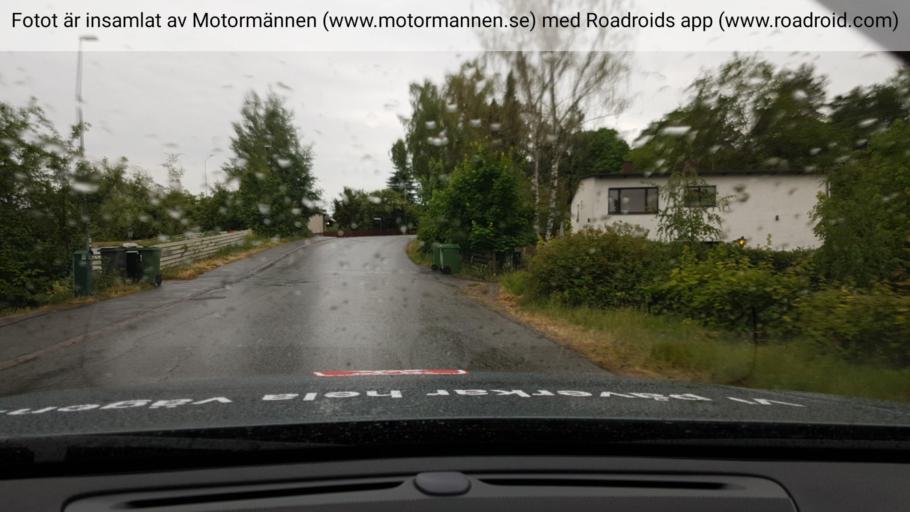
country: SE
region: Stockholm
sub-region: Vallentuna Kommun
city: Vallentuna
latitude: 59.5158
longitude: 18.0630
